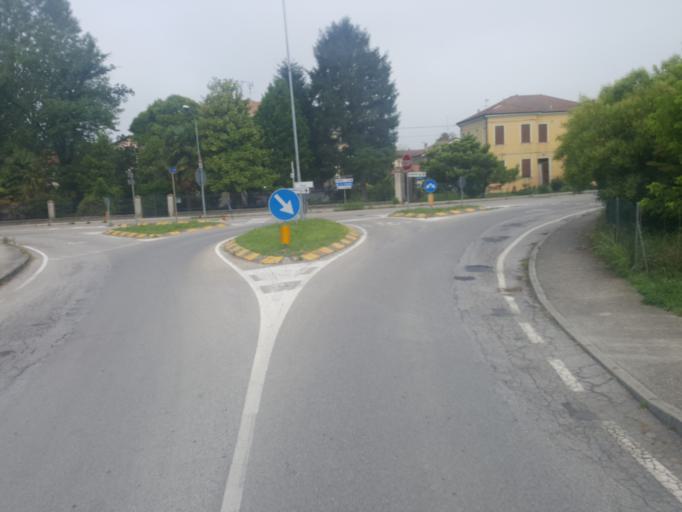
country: IT
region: Veneto
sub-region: Provincia di Rovigo
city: Canaro
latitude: 44.9322
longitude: 11.6764
